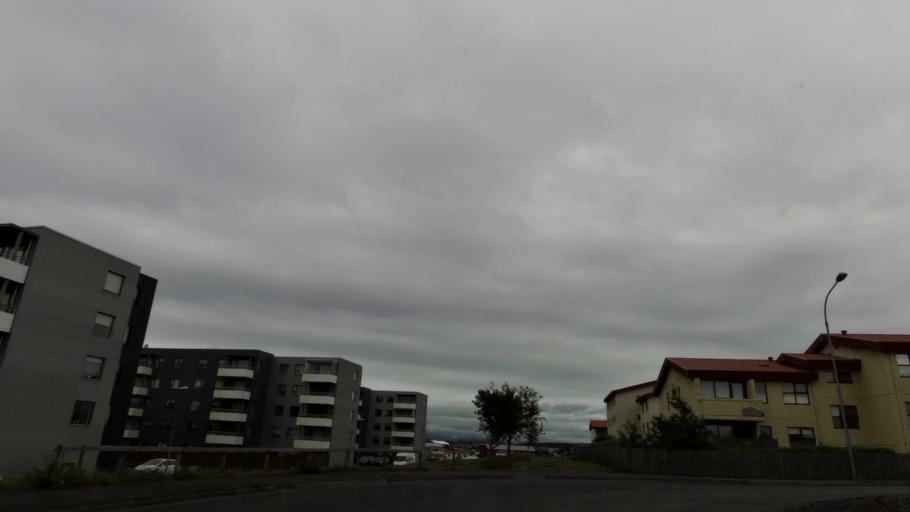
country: IS
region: Capital Region
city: Hafnarfjoerdur
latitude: 64.0593
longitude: -21.9717
